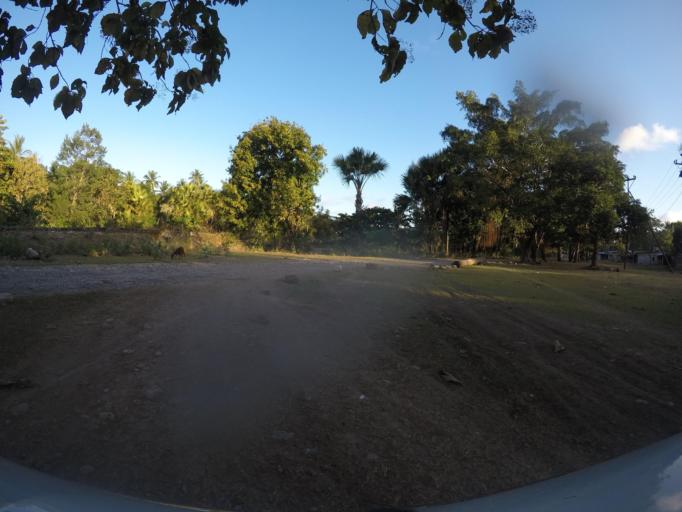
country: TL
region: Baucau
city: Venilale
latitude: -8.7365
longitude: 126.7150
